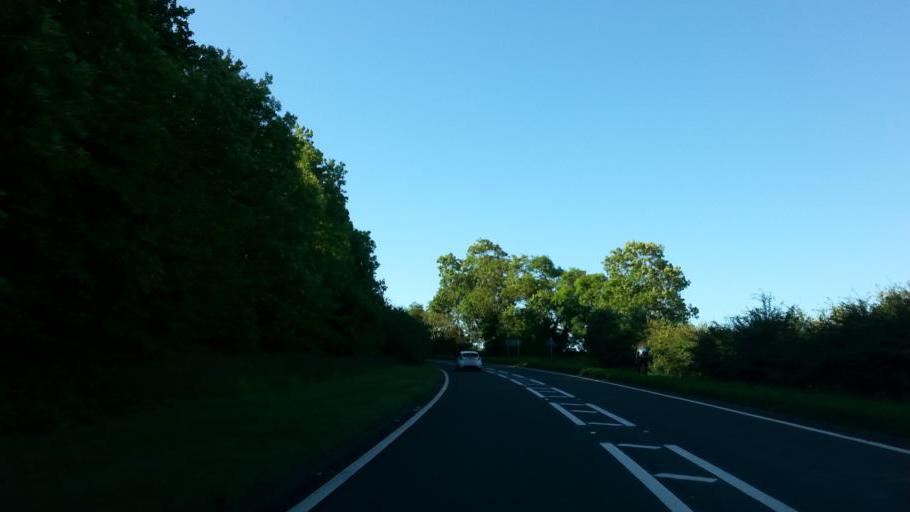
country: GB
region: England
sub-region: Lincolnshire
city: Stamford
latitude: 52.6357
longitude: -0.4932
